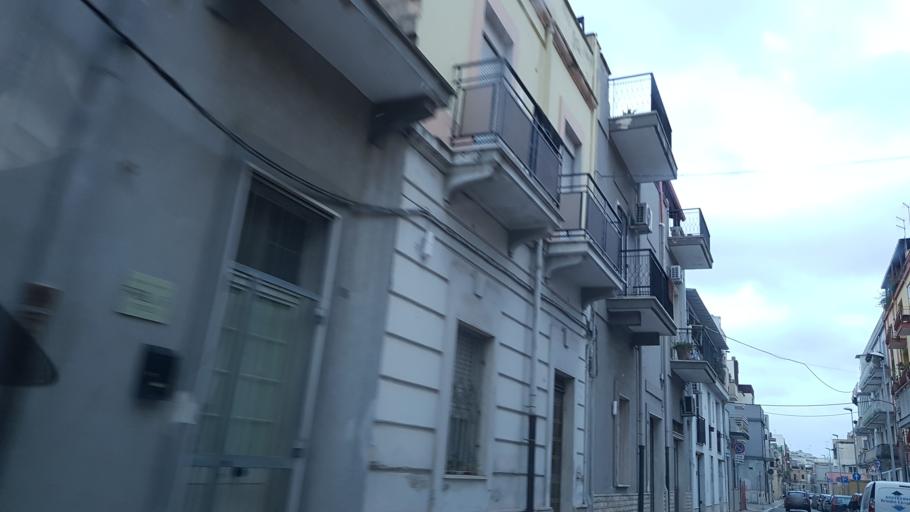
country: IT
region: Apulia
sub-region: Provincia di Brindisi
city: Brindisi
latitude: 40.6330
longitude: 17.9294
